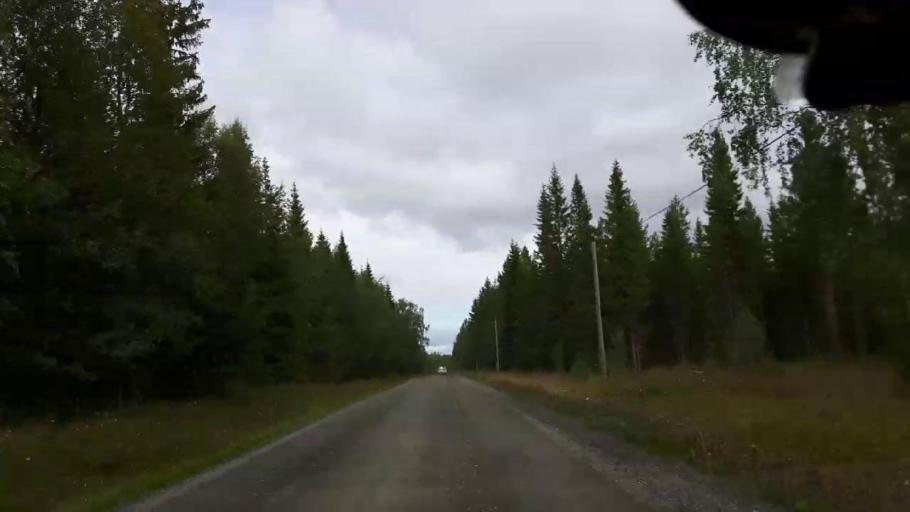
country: SE
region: Jaemtland
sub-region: Krokoms Kommun
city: Valla
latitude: 63.3977
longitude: 14.0988
